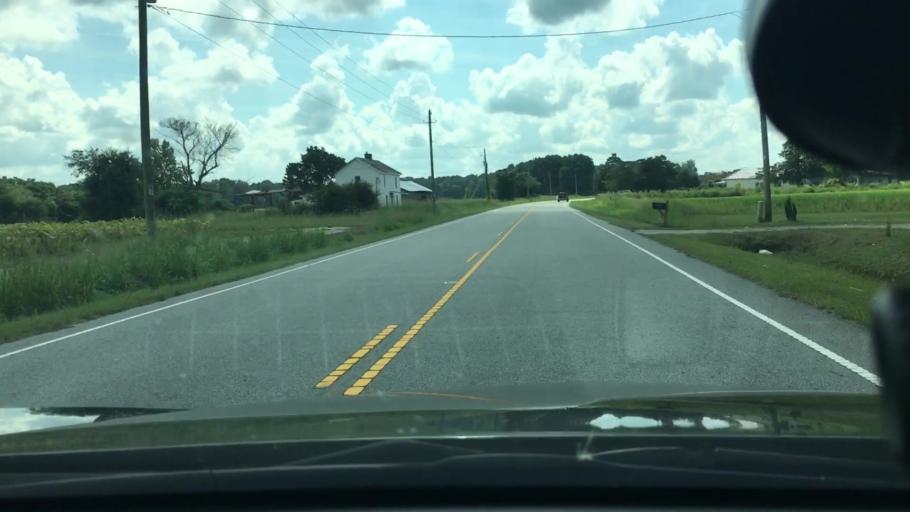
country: US
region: North Carolina
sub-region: Pitt County
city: Farmville
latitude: 35.7114
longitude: -77.5213
